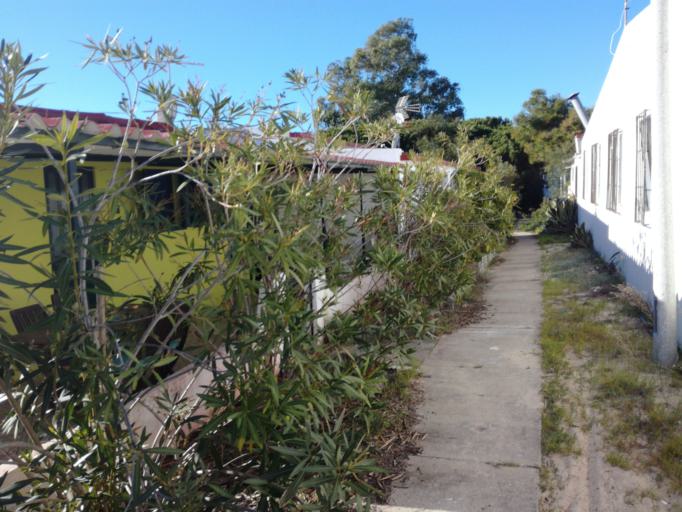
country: PT
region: Faro
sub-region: Olhao
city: Olhao
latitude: 37.0180
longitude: -7.8008
